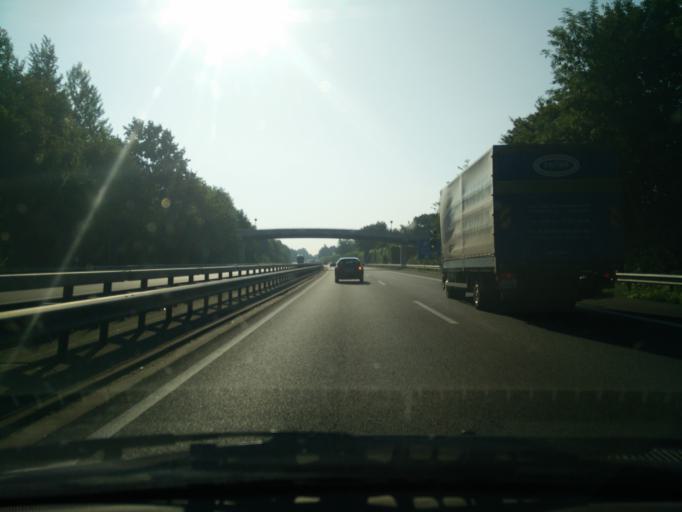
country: DE
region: Schleswig-Holstein
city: Halstenbek
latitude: 53.6357
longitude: 9.8497
